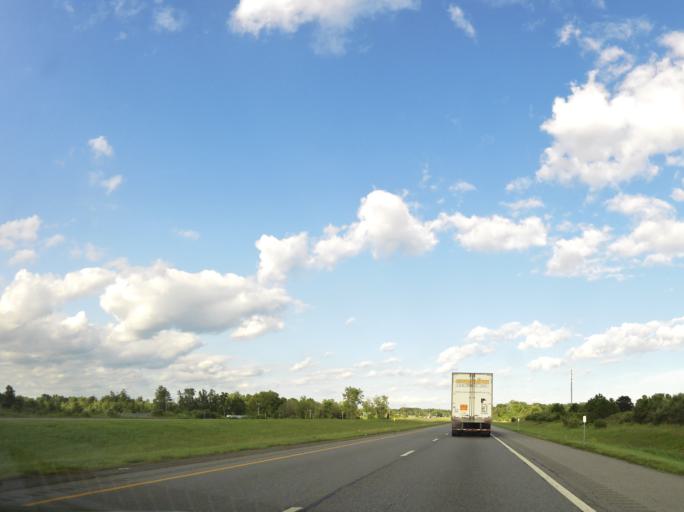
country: US
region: New York
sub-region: Genesee County
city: Oakfield
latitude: 43.0162
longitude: -78.2696
